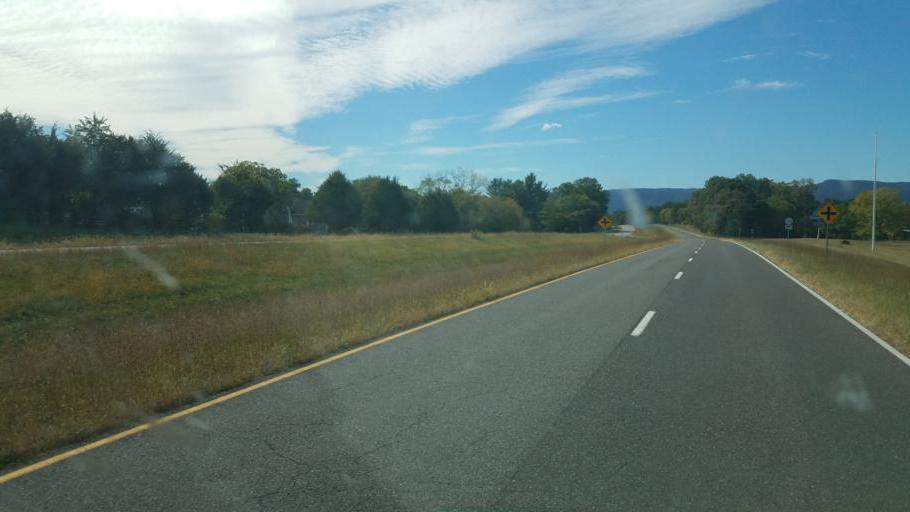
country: US
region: Virginia
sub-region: Page County
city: Luray
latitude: 38.6762
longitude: -78.4233
